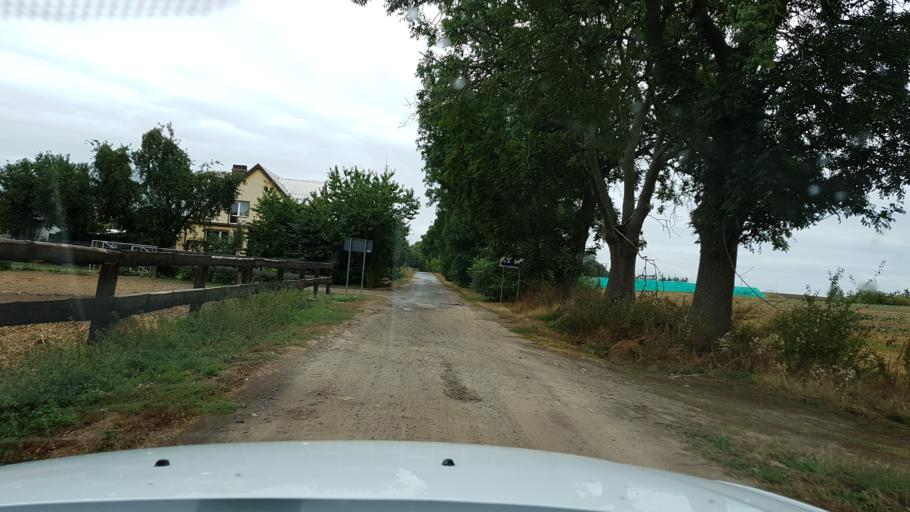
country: PL
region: West Pomeranian Voivodeship
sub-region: Powiat gryfinski
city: Moryn
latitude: 52.8452
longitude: 14.2995
